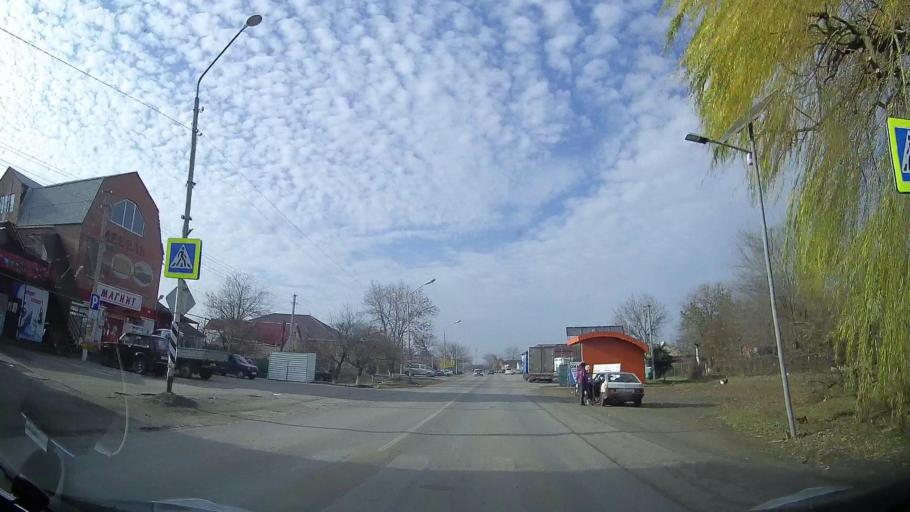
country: RU
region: Rostov
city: Veselyy
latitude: 47.0909
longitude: 40.7444
